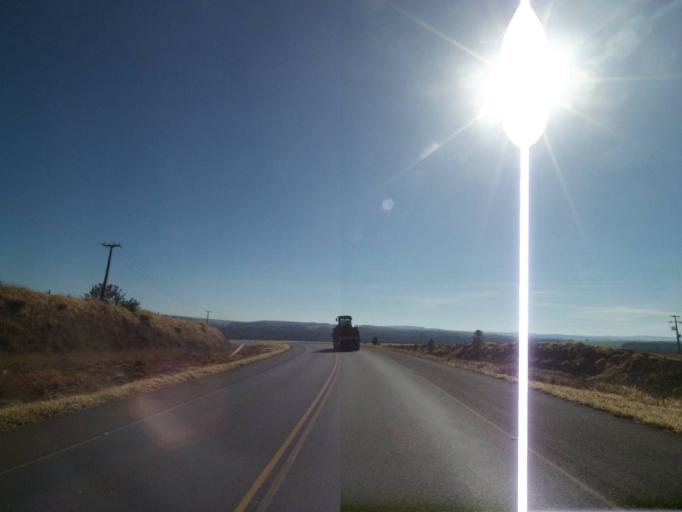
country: BR
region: Parana
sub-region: Tibagi
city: Tibagi
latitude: -24.4886
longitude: -50.4383
